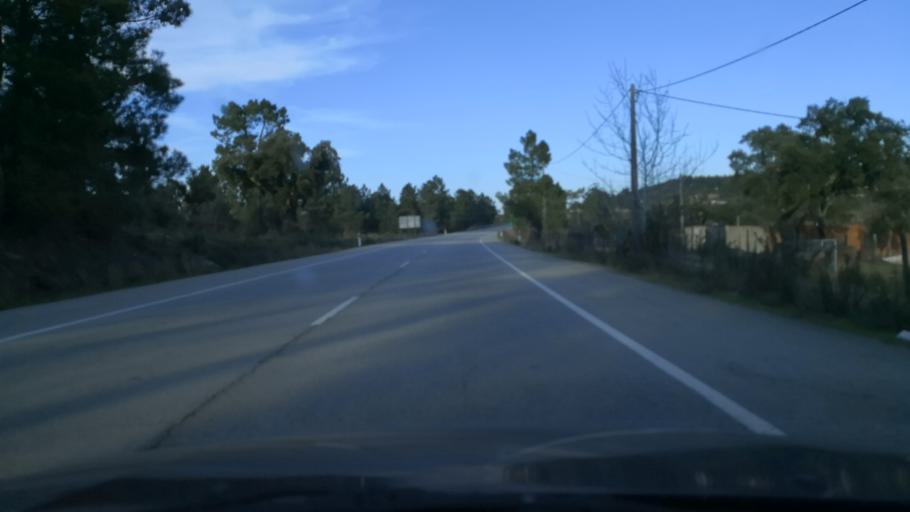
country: PT
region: Castelo Branco
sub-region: Castelo Branco
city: Castelo Branco
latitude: 39.7657
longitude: -7.5957
